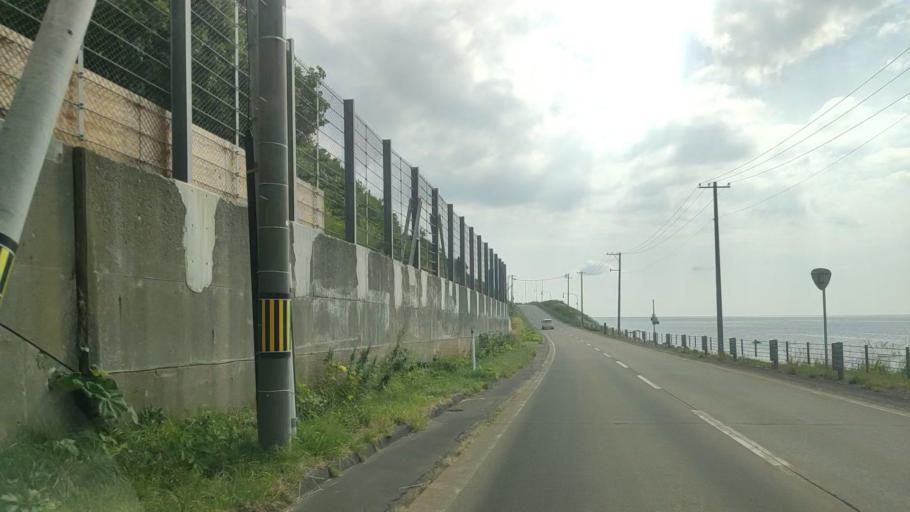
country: JP
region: Hokkaido
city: Rumoi
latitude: 43.7562
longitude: 141.3537
